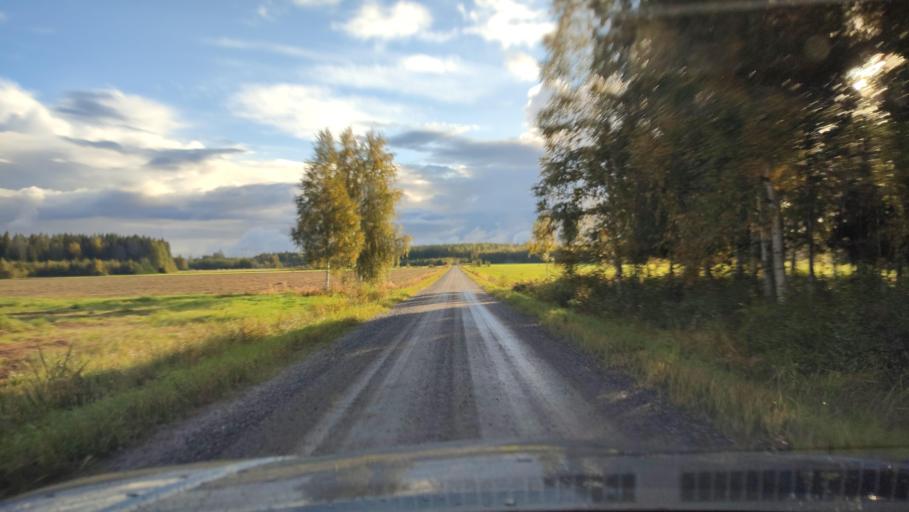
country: FI
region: Southern Ostrobothnia
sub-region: Suupohja
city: Karijoki
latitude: 62.3136
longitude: 21.5532
